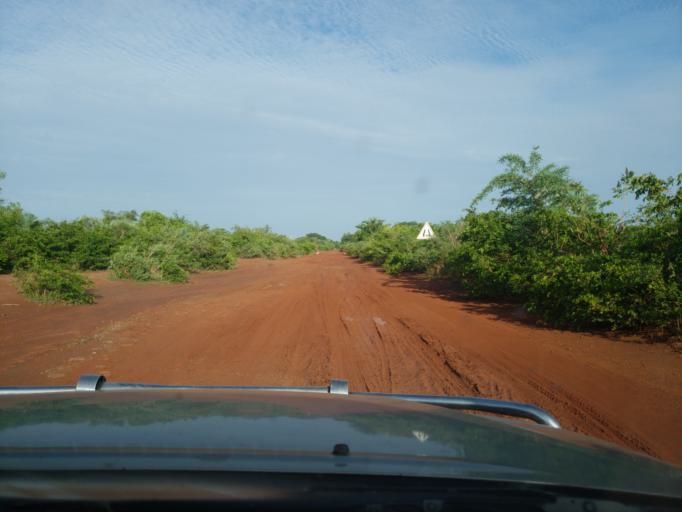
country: ML
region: Sikasso
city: Koutiala
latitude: 12.4250
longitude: -5.6546
